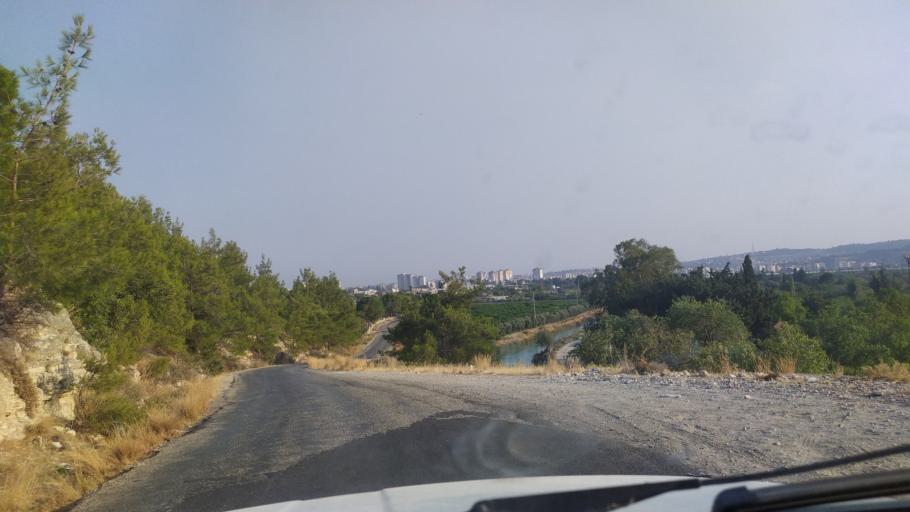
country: TR
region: Mersin
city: Silifke
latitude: 36.4027
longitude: 33.9251
